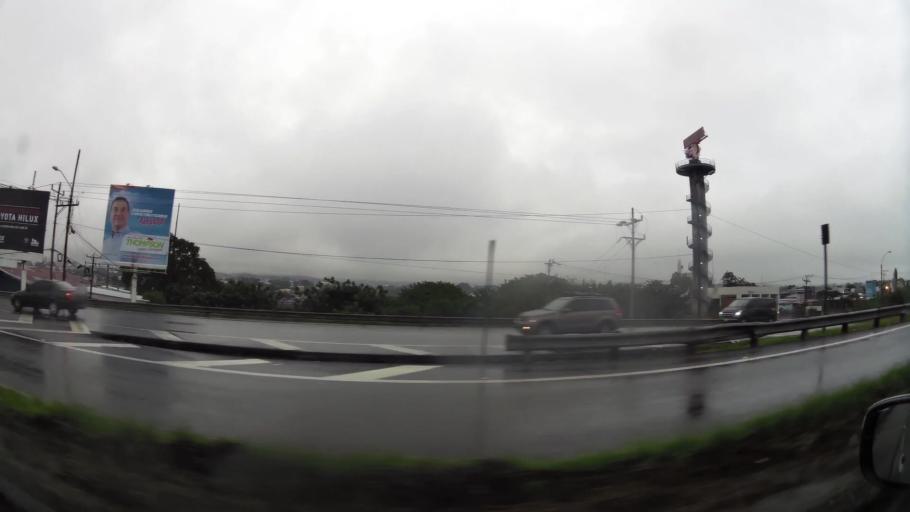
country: CR
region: Alajuela
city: Alajuela
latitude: 9.9999
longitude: -84.2022
